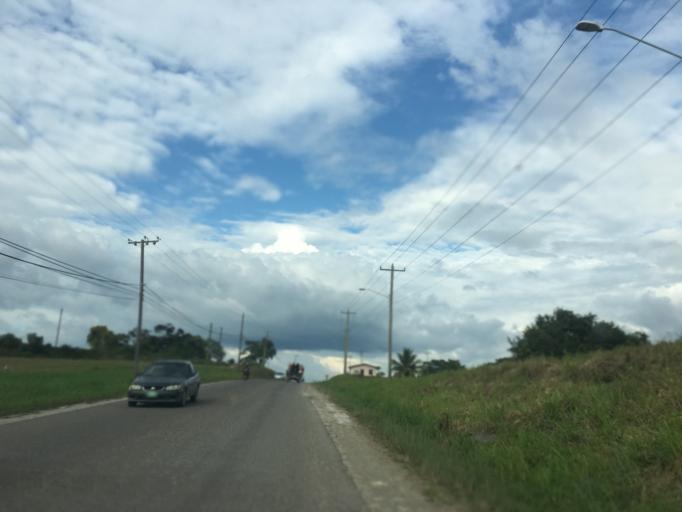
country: BZ
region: Cayo
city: San Ignacio
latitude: 17.1450
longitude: -89.0821
